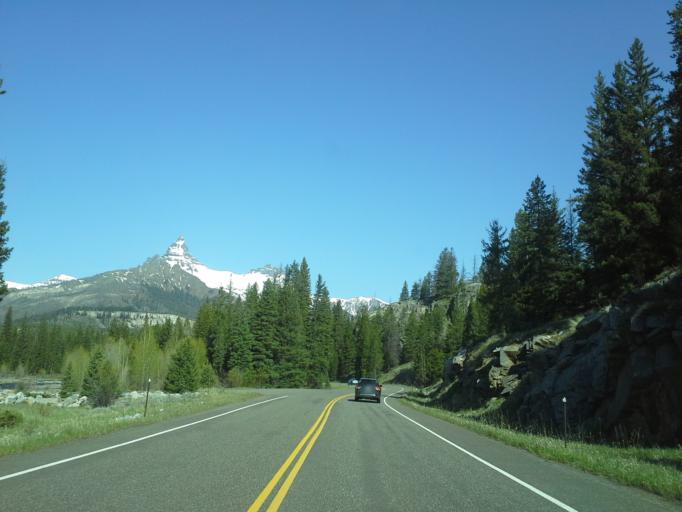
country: US
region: Montana
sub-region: Carbon County
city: Red Lodge
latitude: 44.9556
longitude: -109.7995
